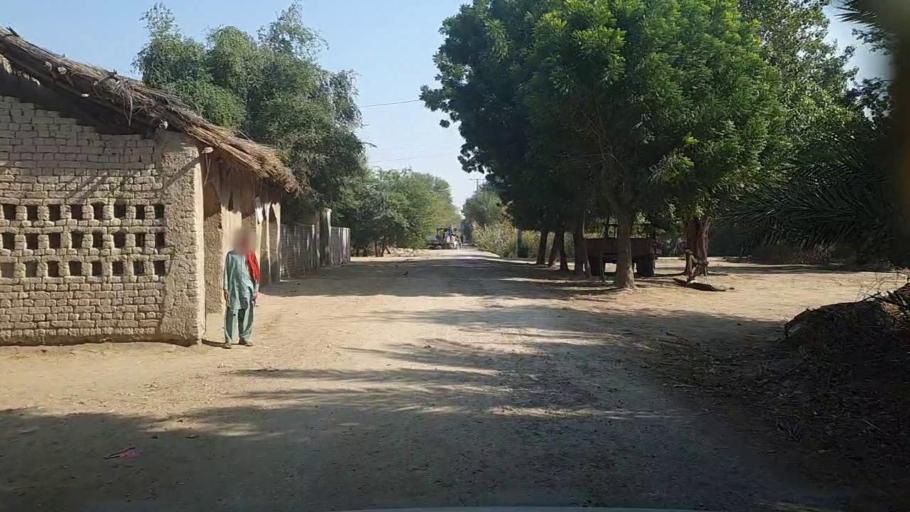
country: PK
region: Sindh
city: Kandiari
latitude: 26.9411
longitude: 68.5382
